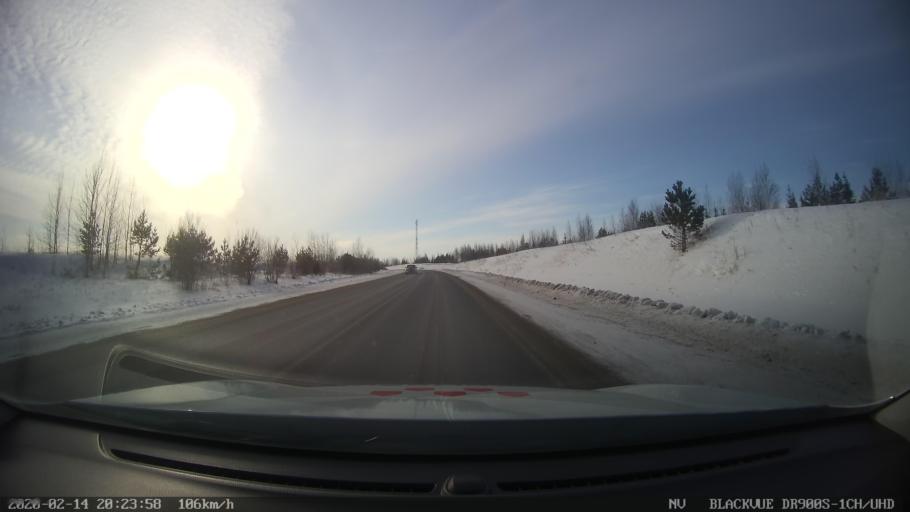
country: RU
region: Tatarstan
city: Verkhniy Uslon
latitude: 55.5197
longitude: 48.9675
